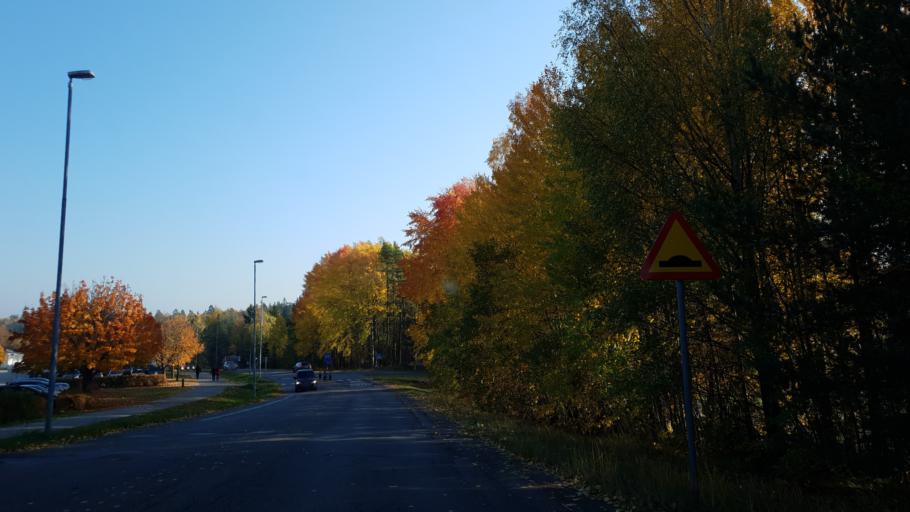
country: SE
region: Stockholm
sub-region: Haninge Kommun
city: Haninge
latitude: 59.1703
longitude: 18.1932
